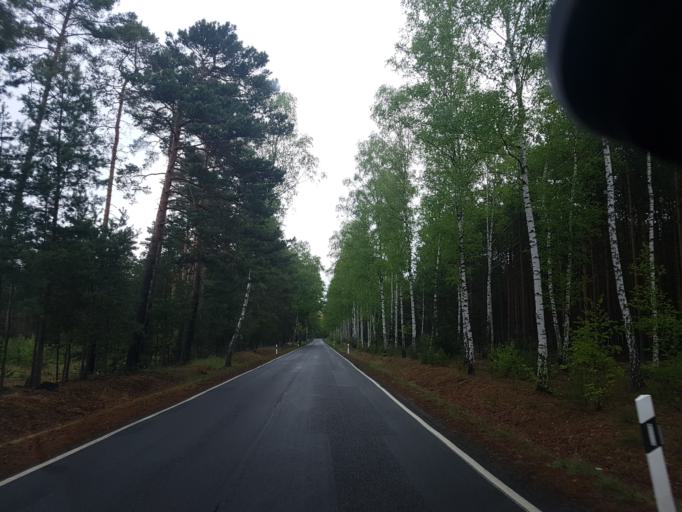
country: DE
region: Brandenburg
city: Spremberg
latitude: 51.6226
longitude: 14.4189
